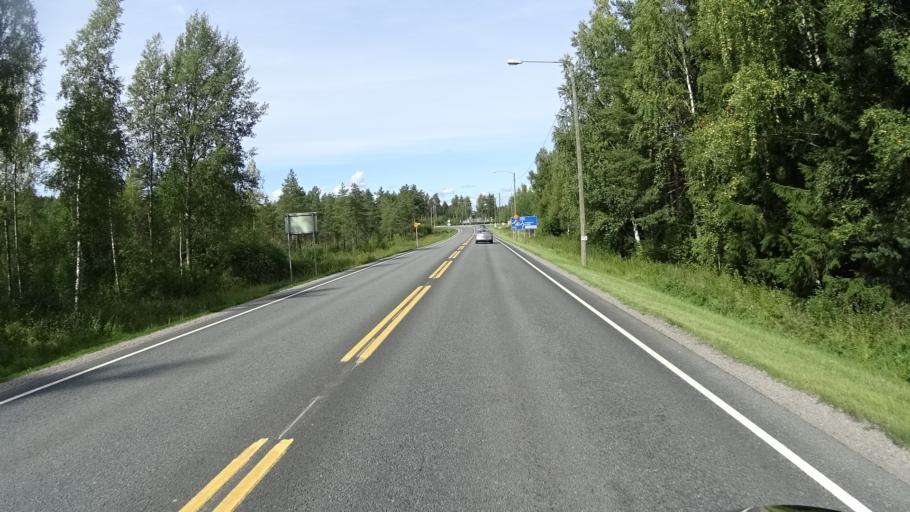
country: FI
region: Pirkanmaa
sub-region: Tampere
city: Haemeenkyroe
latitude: 61.6521
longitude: 23.1780
